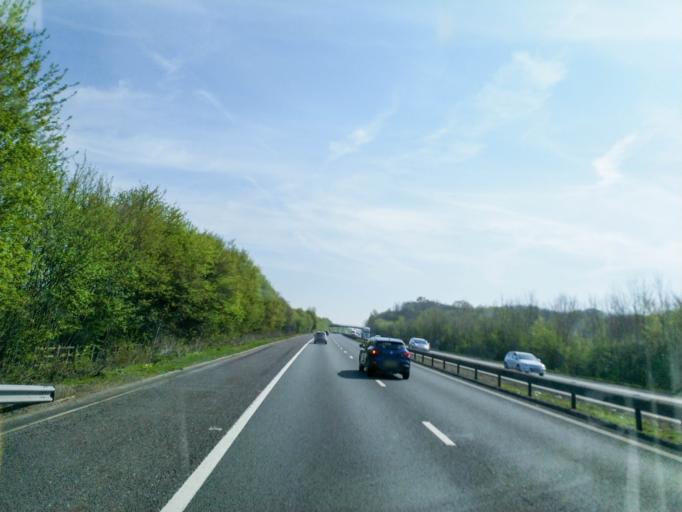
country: GB
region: England
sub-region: Kent
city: Kemsing
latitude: 51.3010
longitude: 0.2349
